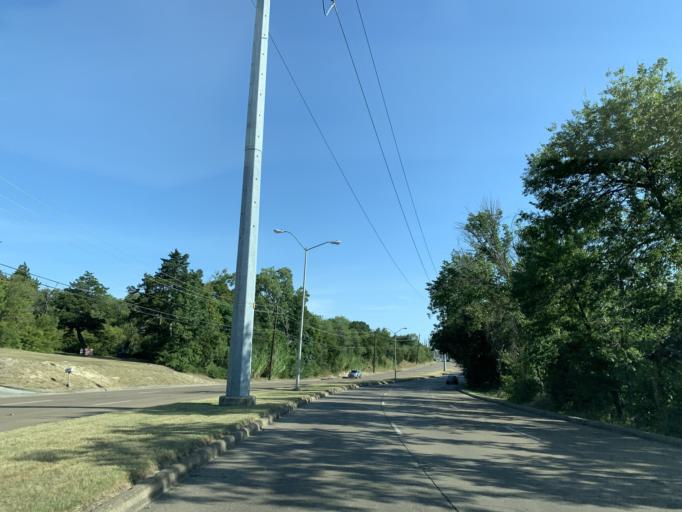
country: US
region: Texas
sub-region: Dallas County
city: Cockrell Hill
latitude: 32.6996
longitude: -96.8912
